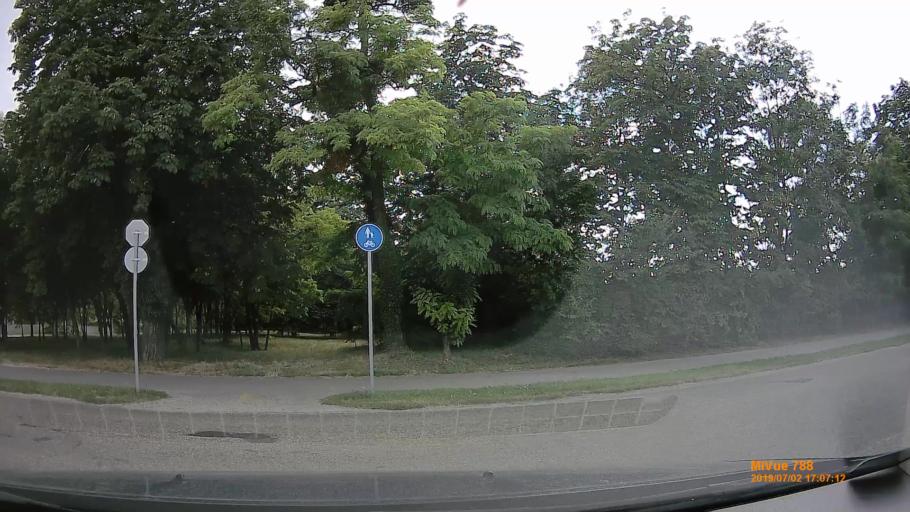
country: HU
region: Gyor-Moson-Sopron
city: Mosonmagyarovar
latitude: 47.8749
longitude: 17.2852
